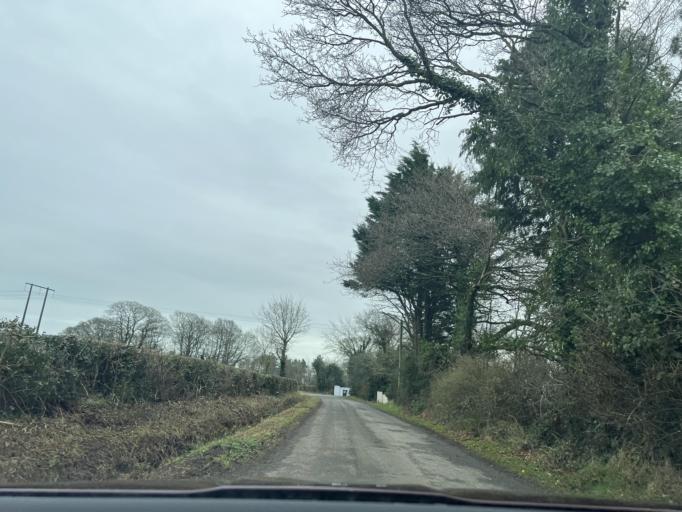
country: IE
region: Leinster
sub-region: Loch Garman
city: Castlebridge
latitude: 52.3864
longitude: -6.5288
